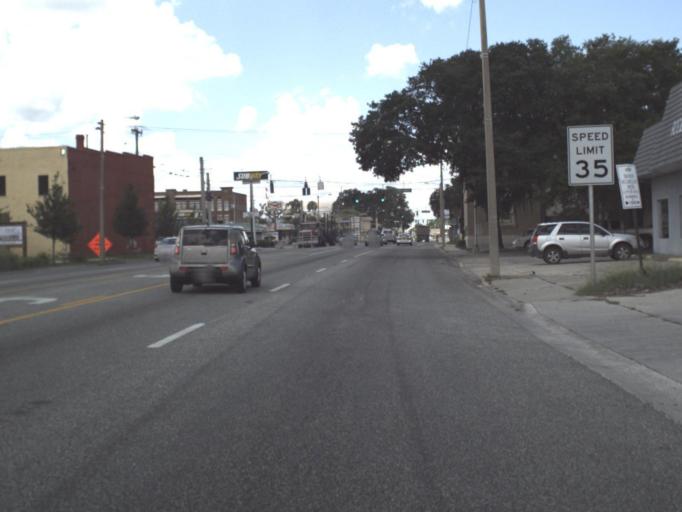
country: US
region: Florida
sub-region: Putnam County
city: Palatka
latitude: 29.6471
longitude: -81.6287
